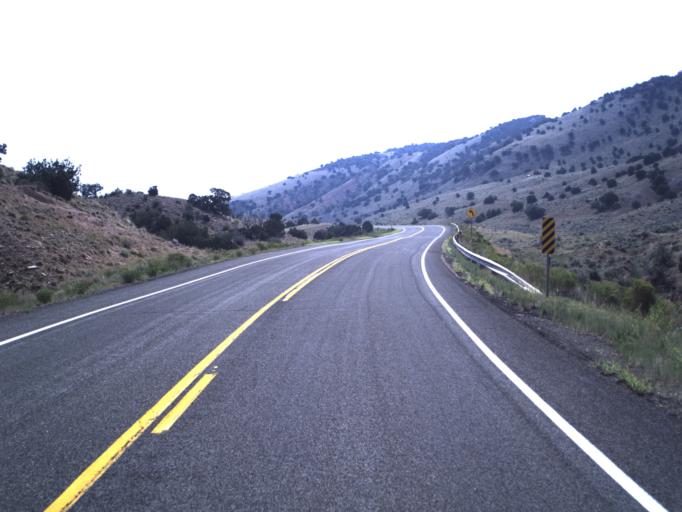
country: US
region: Utah
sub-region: Daggett County
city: Manila
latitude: 40.9320
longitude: -109.7108
